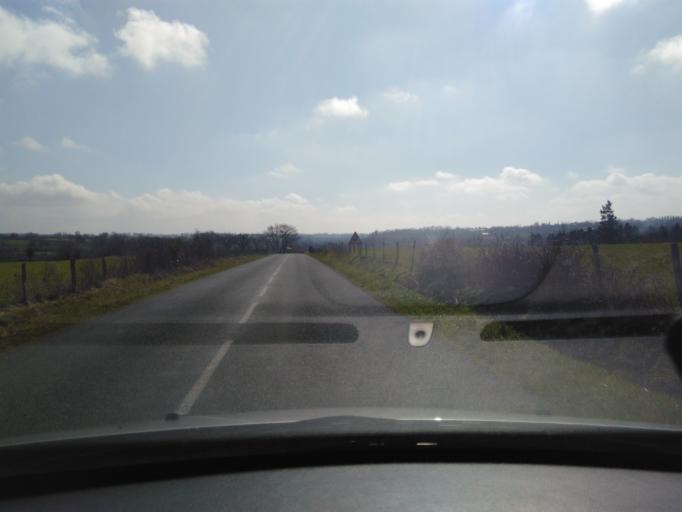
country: FR
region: Pays de la Loire
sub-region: Departement de la Vendee
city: Sainte-Cecile
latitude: 46.7065
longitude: -1.1180
